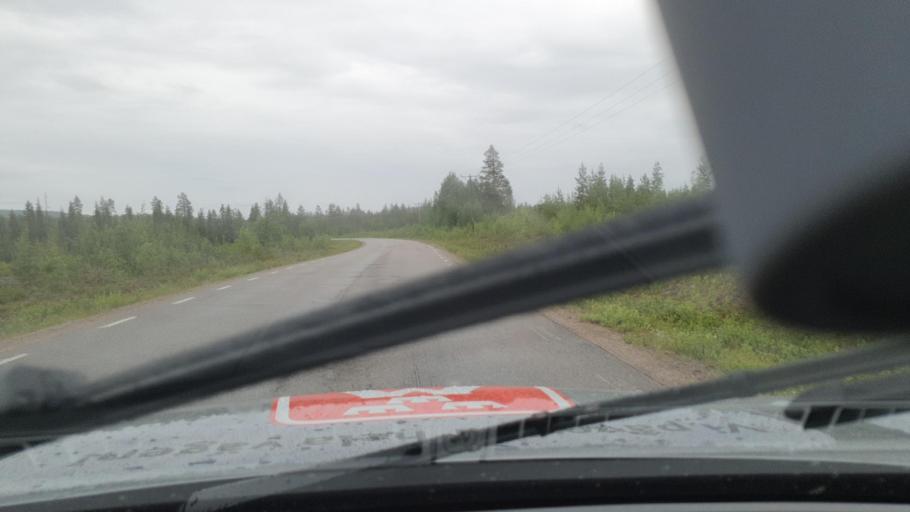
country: SE
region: Norrbotten
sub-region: Pajala Kommun
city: Pajala
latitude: 66.7846
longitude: 23.1311
